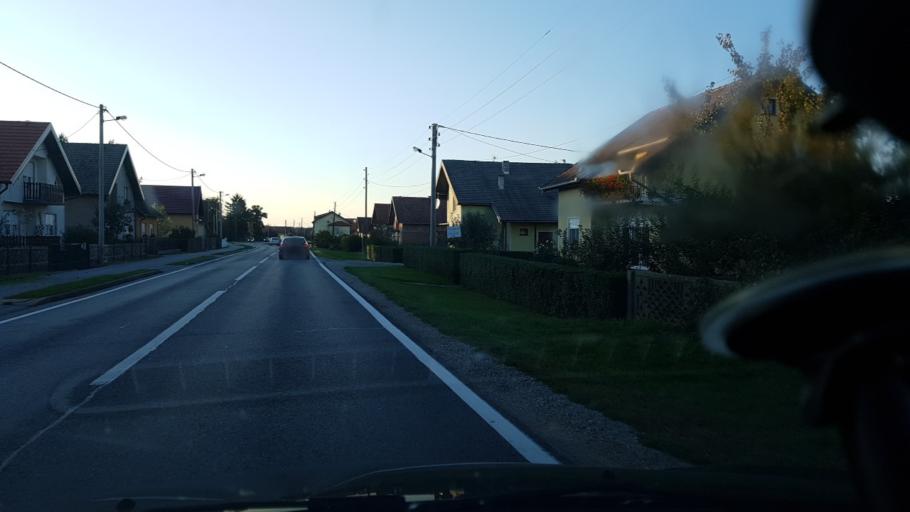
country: HR
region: Koprivnicko-Krizevacka
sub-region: Grad Koprivnica
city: Koprivnica
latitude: 46.1338
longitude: 16.8637
